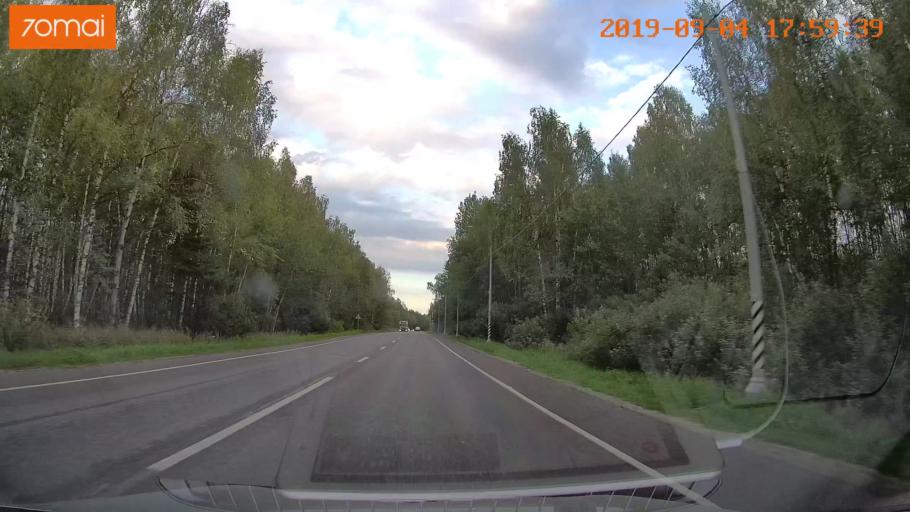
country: RU
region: Moskovskaya
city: Il'inskiy Pogost
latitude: 55.4918
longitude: 38.8438
